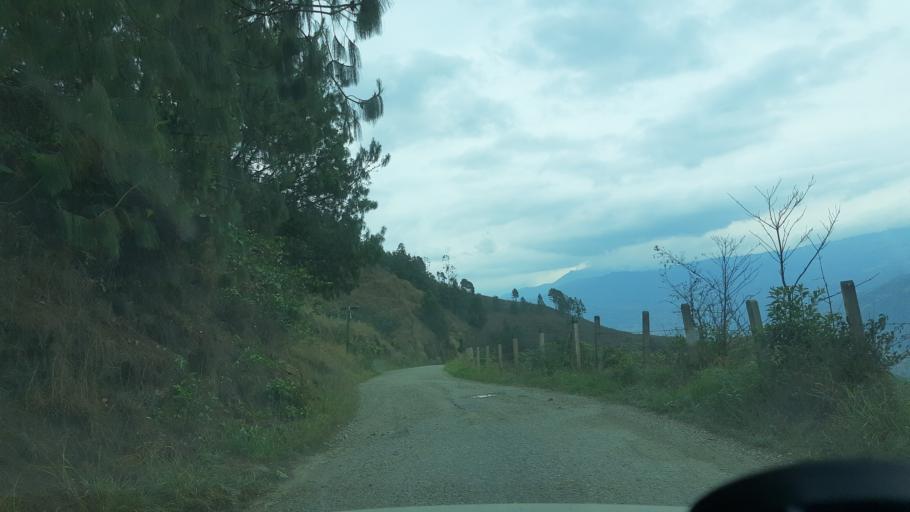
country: CO
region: Boyaca
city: Somondoco
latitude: 4.9778
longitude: -73.3782
